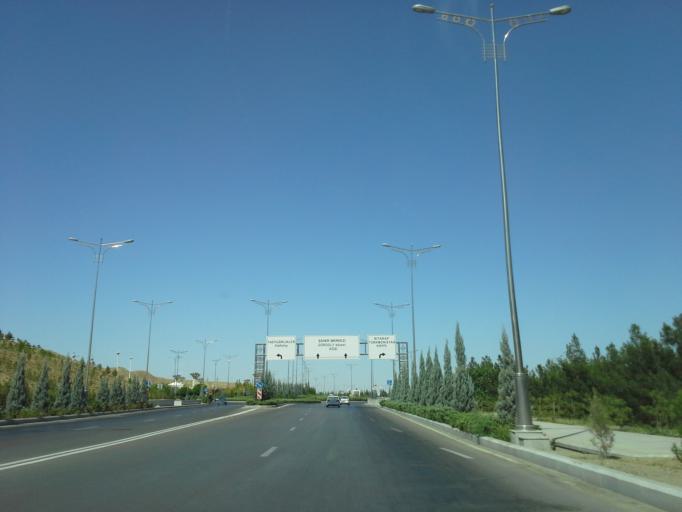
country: TM
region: Ahal
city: Ashgabat
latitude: 37.9303
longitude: 58.3172
